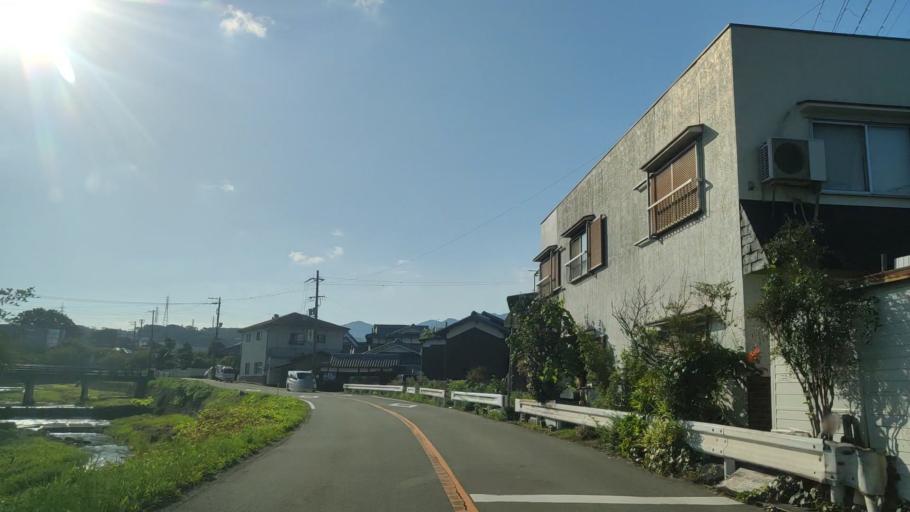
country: JP
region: Hyogo
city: Sandacho
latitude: 34.8273
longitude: 135.2410
